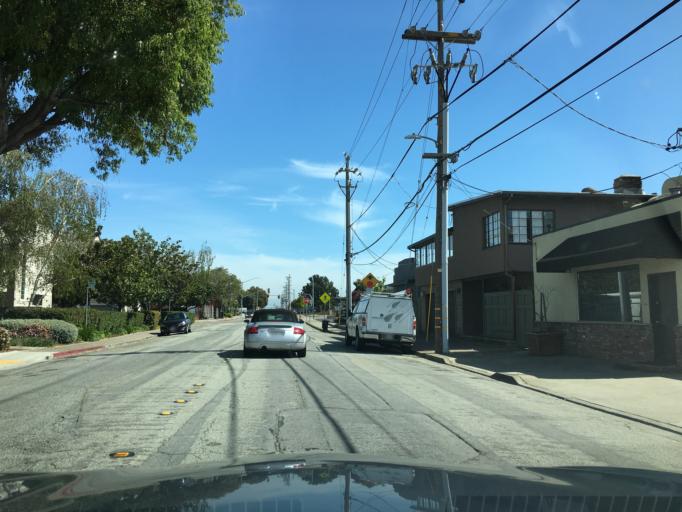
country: US
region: California
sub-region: San Mateo County
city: Belmont
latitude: 37.5221
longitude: -122.2768
